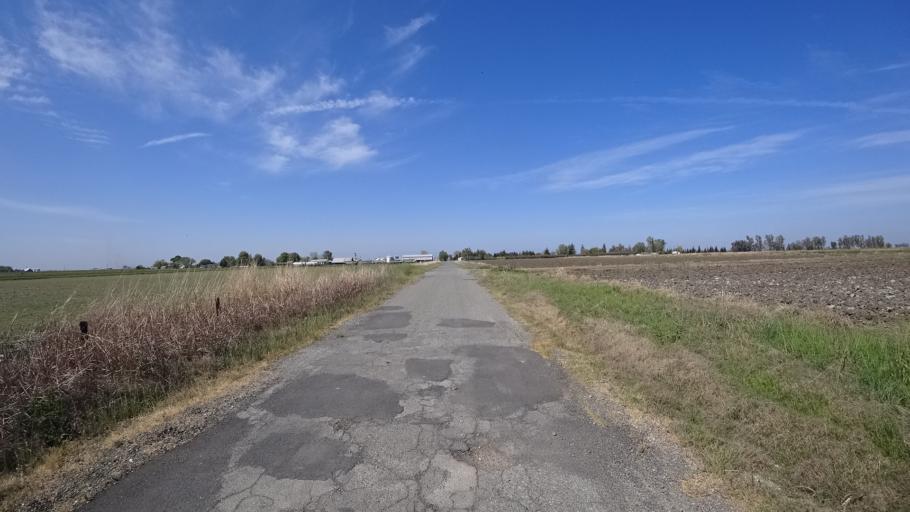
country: US
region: California
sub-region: Glenn County
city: Hamilton City
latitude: 39.5800
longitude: -122.0323
